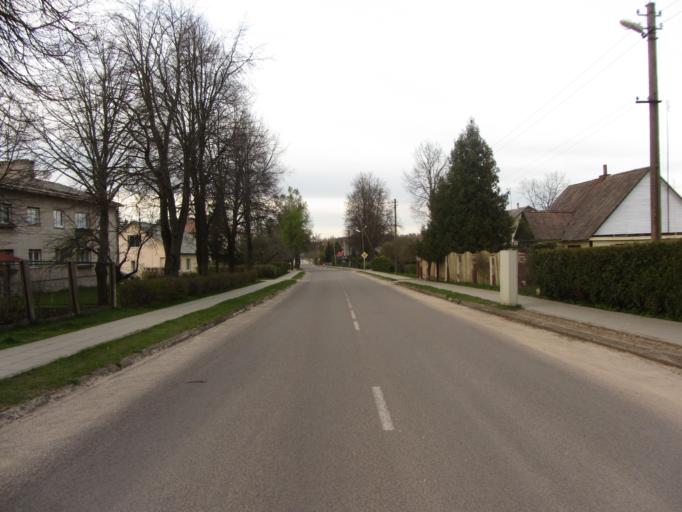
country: LT
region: Utenos apskritis
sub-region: Utena
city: Utena
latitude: 55.7367
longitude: 25.8327
